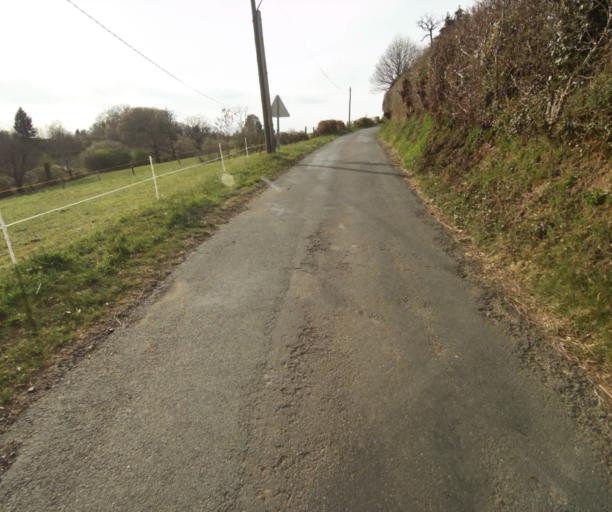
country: FR
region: Limousin
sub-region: Departement de la Correze
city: Naves
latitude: 45.3213
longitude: 1.7443
